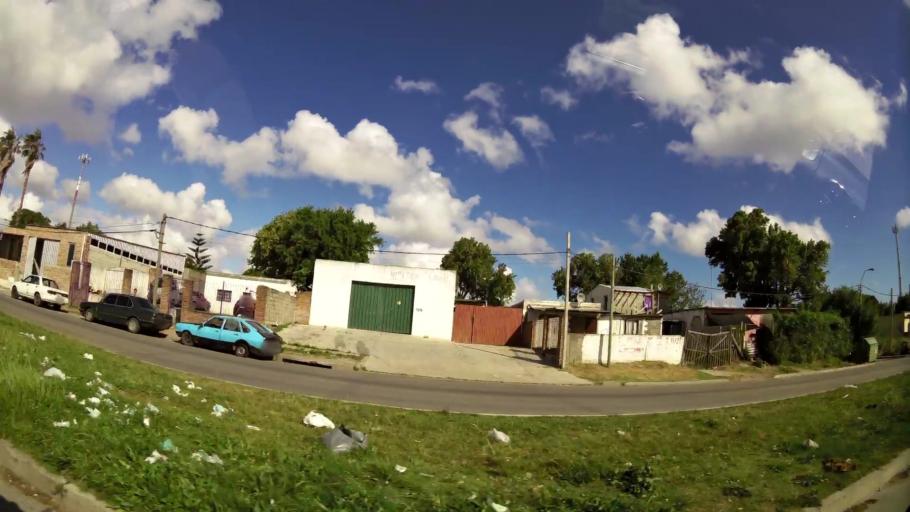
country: UY
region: Canelones
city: La Paz
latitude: -34.8145
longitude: -56.2316
